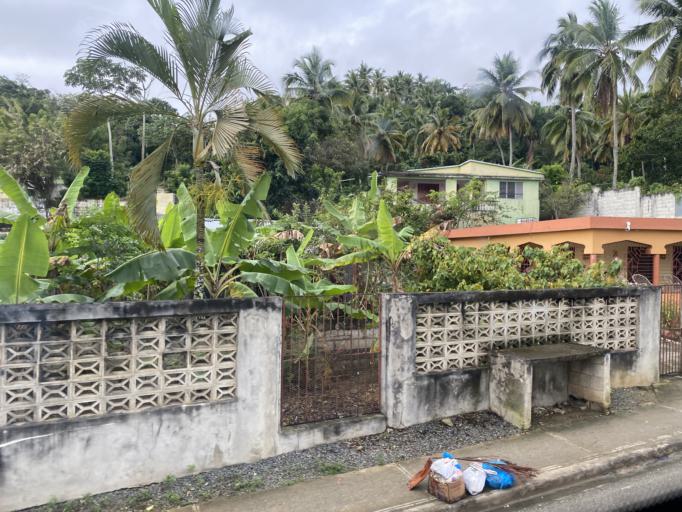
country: DO
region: El Seibo
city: Miches
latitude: 18.9848
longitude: -69.0520
